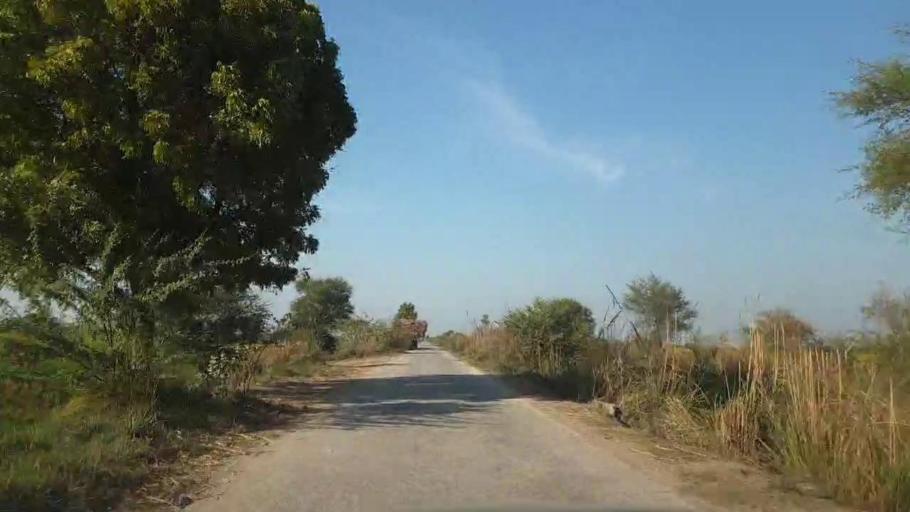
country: PK
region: Sindh
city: Tando Adam
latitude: 25.7236
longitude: 68.7029
